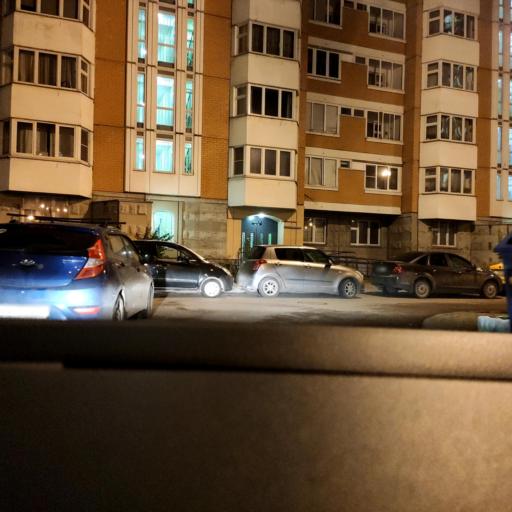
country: RU
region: Moscow
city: Vostochnyy
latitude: 55.8209
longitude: 37.8904
